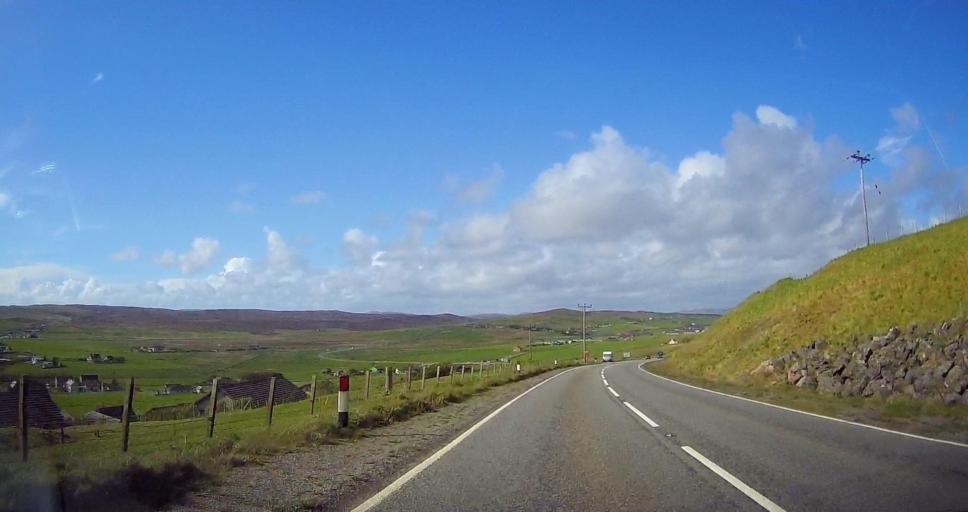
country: GB
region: Scotland
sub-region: Shetland Islands
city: Lerwick
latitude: 60.1805
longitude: -1.2248
